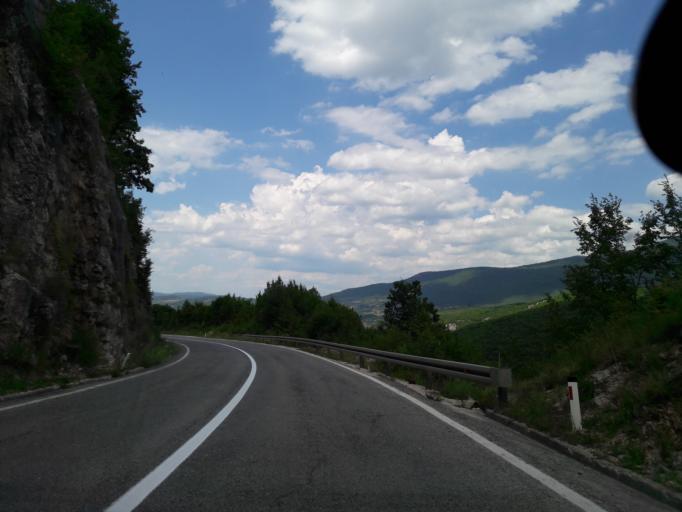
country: BA
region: Republika Srpska
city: Mrkonjic Grad
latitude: 44.4976
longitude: 17.1522
